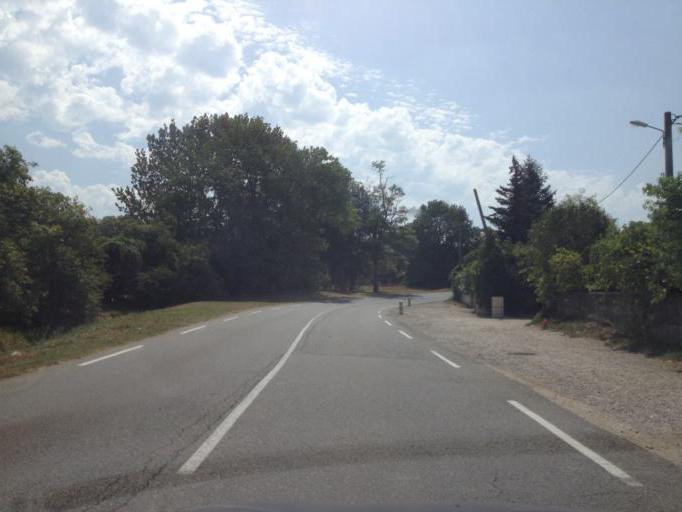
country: FR
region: Rhone-Alpes
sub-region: Departement de la Drome
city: Chatuzange-le-Goubet
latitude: 45.0105
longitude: 5.0885
